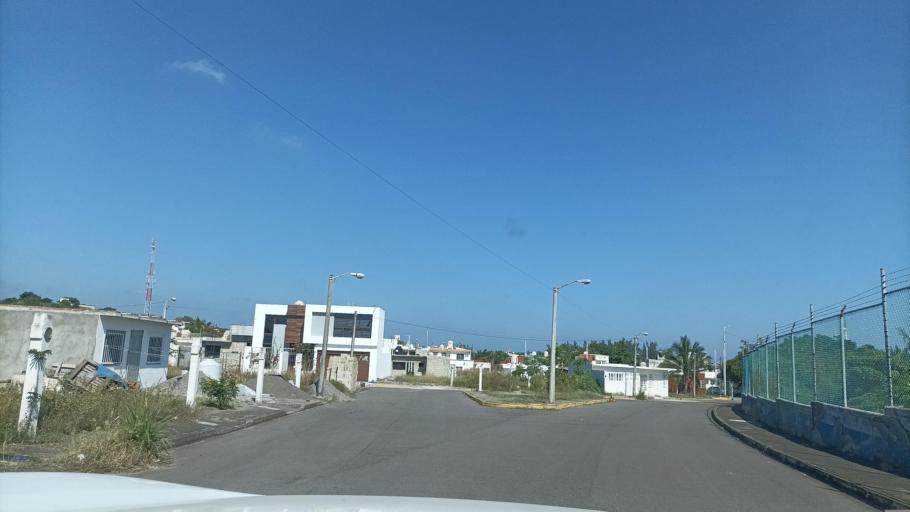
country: MX
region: Veracruz
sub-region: Veracruz
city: Rio Medio [Granja]
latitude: 19.2017
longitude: -96.1797
